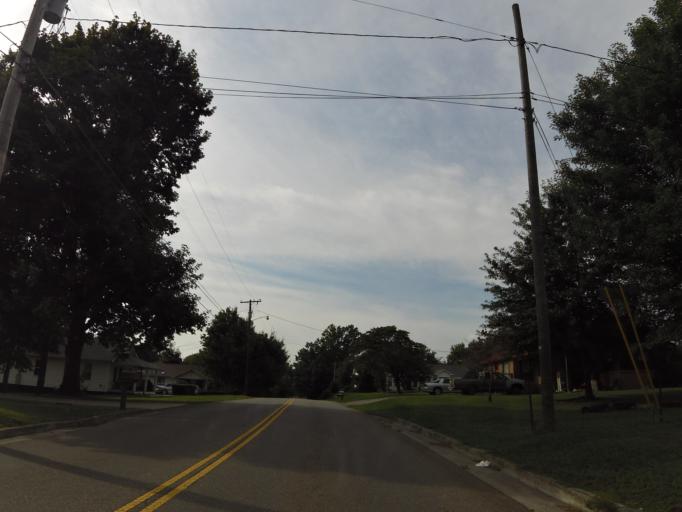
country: US
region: Tennessee
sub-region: Blount County
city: Maryville
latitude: 35.7633
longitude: -83.9520
